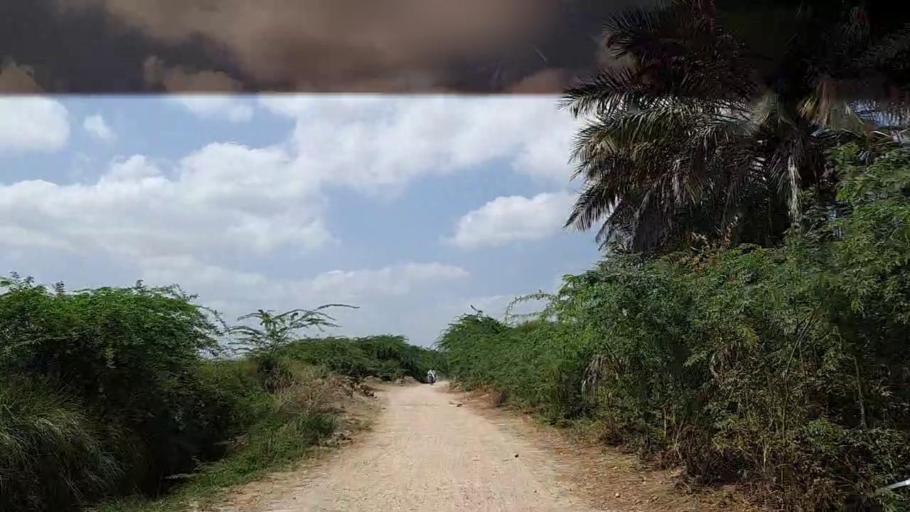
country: PK
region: Sindh
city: Badin
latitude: 24.5956
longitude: 68.7751
